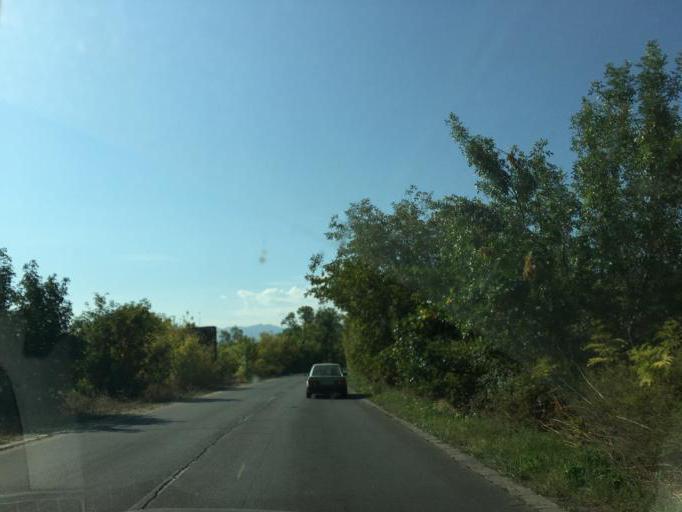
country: BG
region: Pazardzhik
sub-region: Obshtina Pazardzhik
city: Pazardzhik
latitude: 42.1280
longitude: 24.2941
